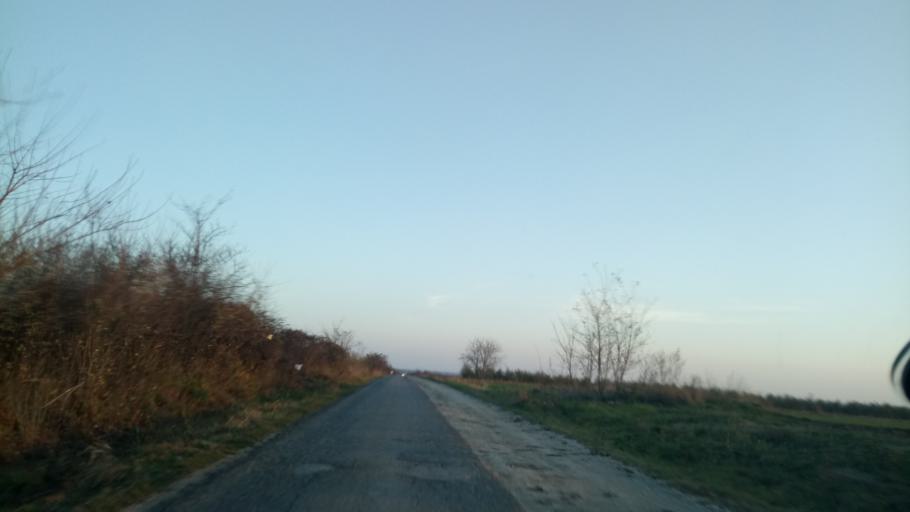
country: RS
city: Novi Slankamen
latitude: 45.1105
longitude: 20.2781
